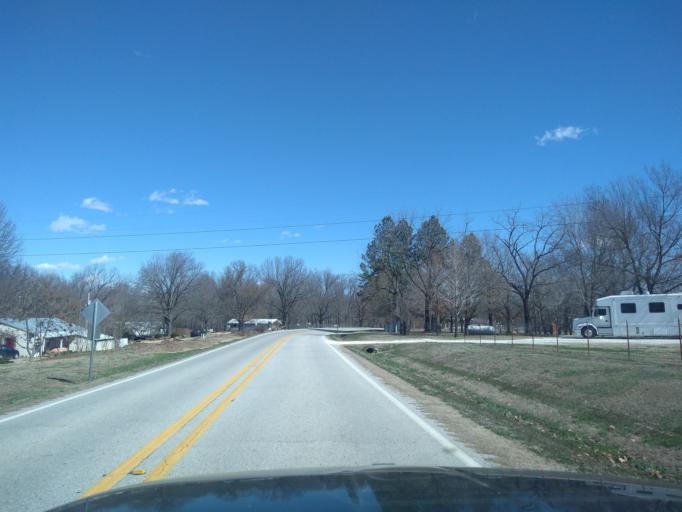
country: US
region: Arkansas
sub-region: Washington County
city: Farmington
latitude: 36.0802
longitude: -94.3049
